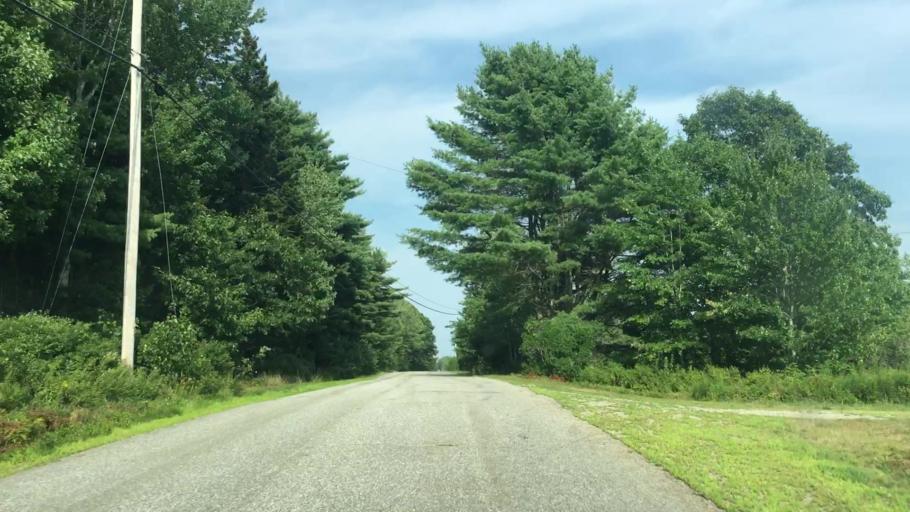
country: US
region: Maine
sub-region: Knox County
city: Friendship
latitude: 44.0336
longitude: -69.3429
